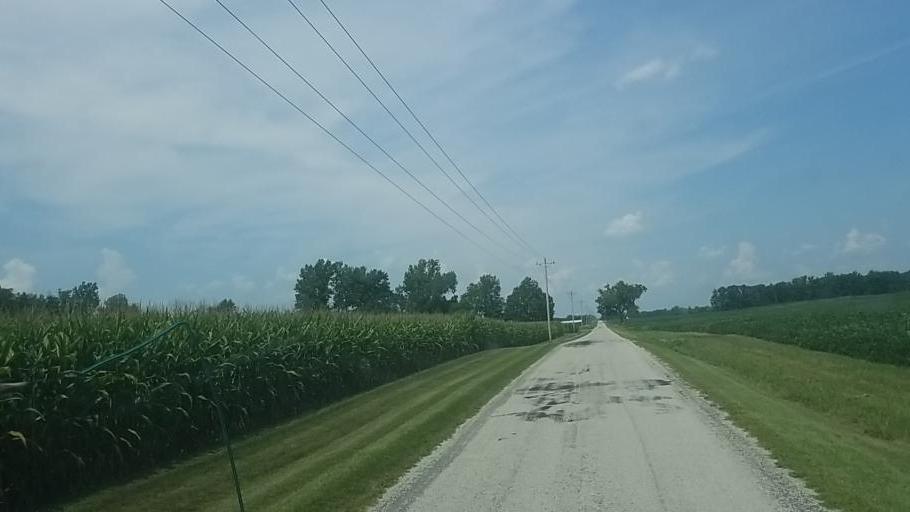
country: US
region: Ohio
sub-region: Wyandot County
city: Upper Sandusky
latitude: 40.6528
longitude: -83.3620
